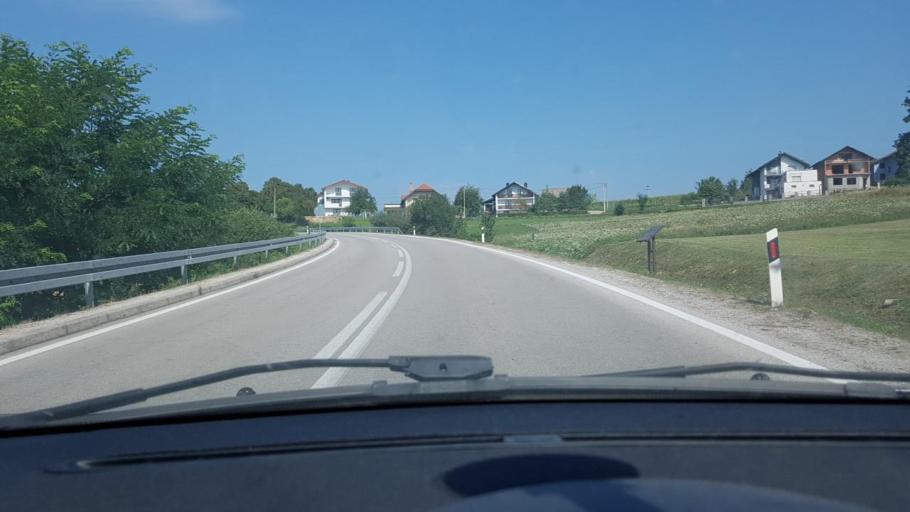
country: BA
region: Federation of Bosnia and Herzegovina
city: Velika Kladusa
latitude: 45.1964
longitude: 15.8082
